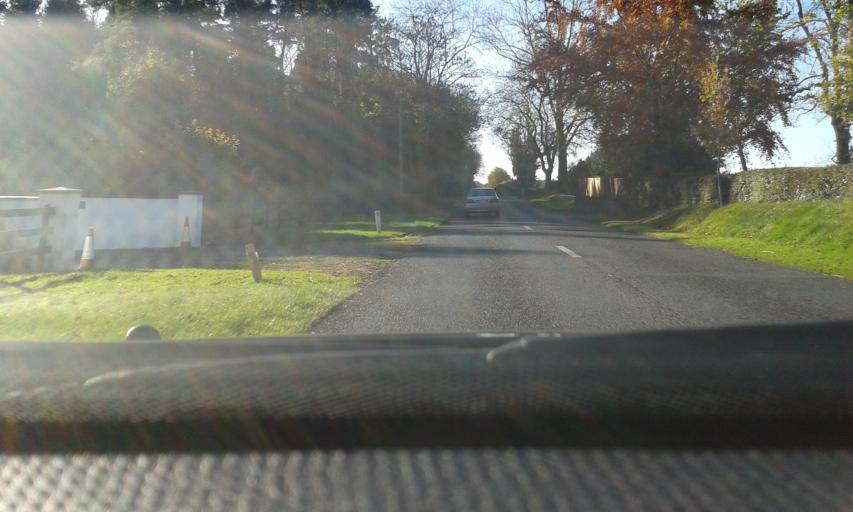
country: IE
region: Leinster
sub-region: Kildare
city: Rathangan
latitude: 53.1907
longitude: -7.0115
